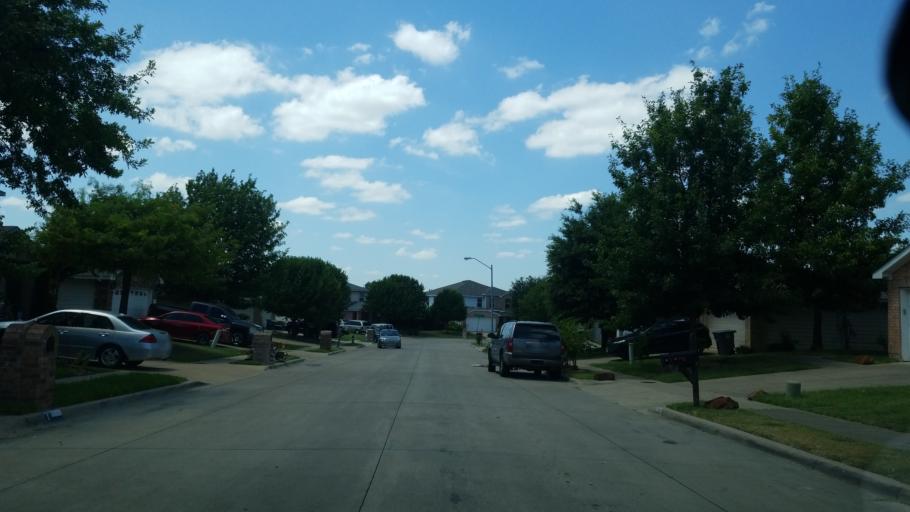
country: US
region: Texas
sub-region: Dallas County
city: Hutchins
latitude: 32.7355
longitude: -96.7133
